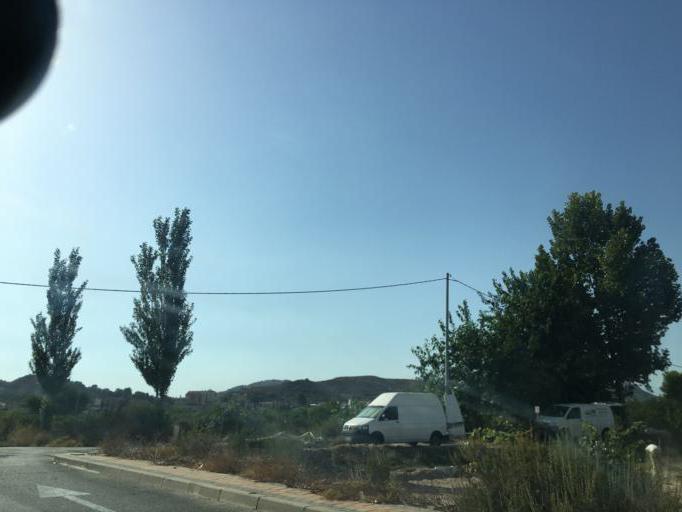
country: ES
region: Murcia
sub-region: Murcia
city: Santomera
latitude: 38.0379
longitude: -1.0761
